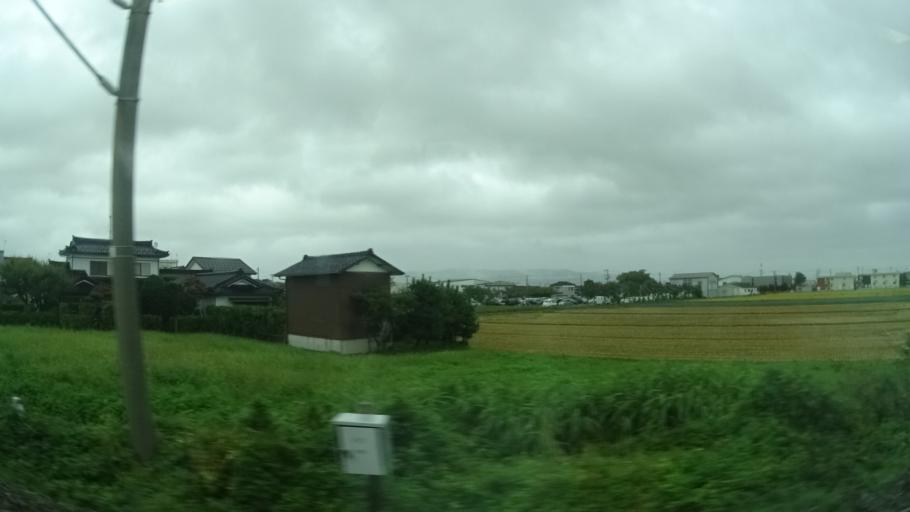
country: JP
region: Yamagata
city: Sakata
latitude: 38.8537
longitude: 139.9072
